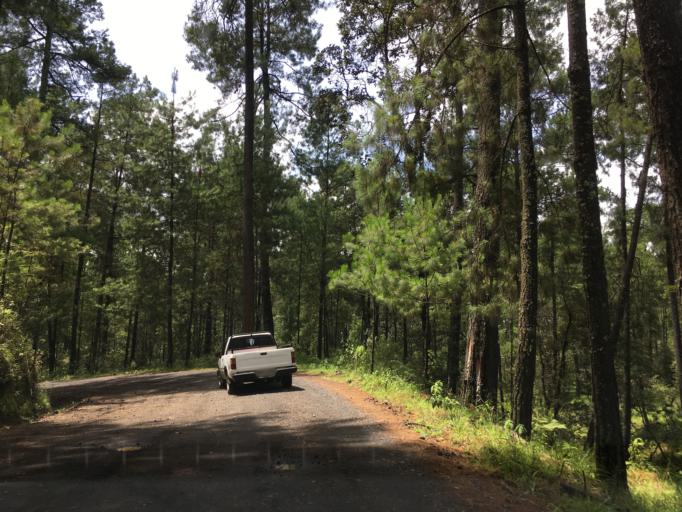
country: MX
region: Michoacan
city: Nuevo San Juan Parangaricutiro
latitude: 19.4479
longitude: -102.1854
